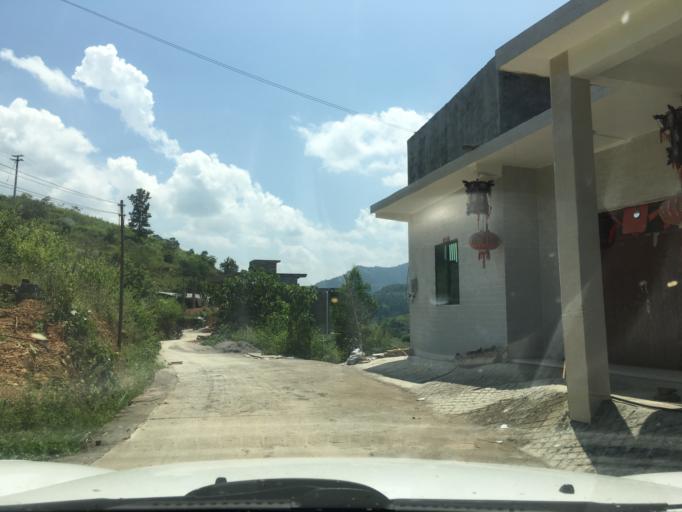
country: CN
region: Guangxi Zhuangzu Zizhiqu
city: Xinzhou
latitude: 25.4577
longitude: 105.7722
